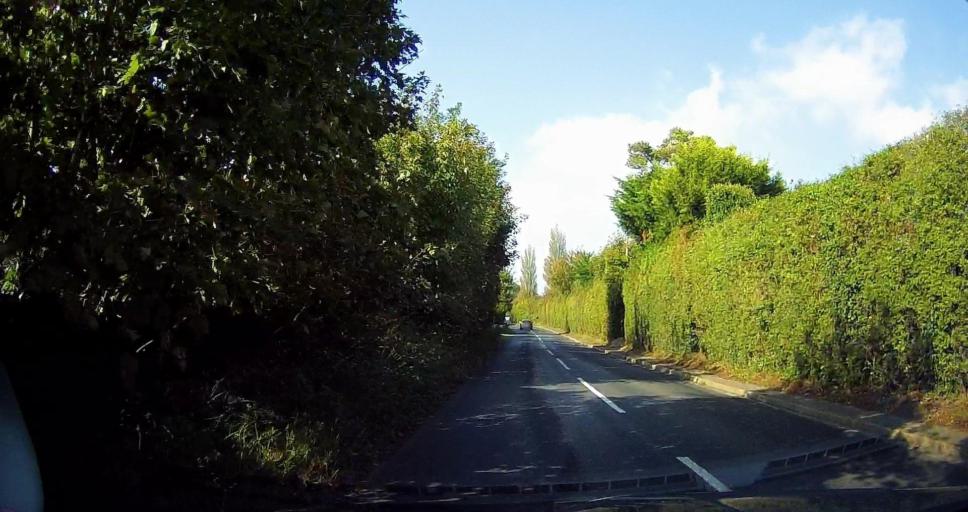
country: GB
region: England
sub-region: Kent
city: Wye
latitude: 51.1821
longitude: 0.9147
